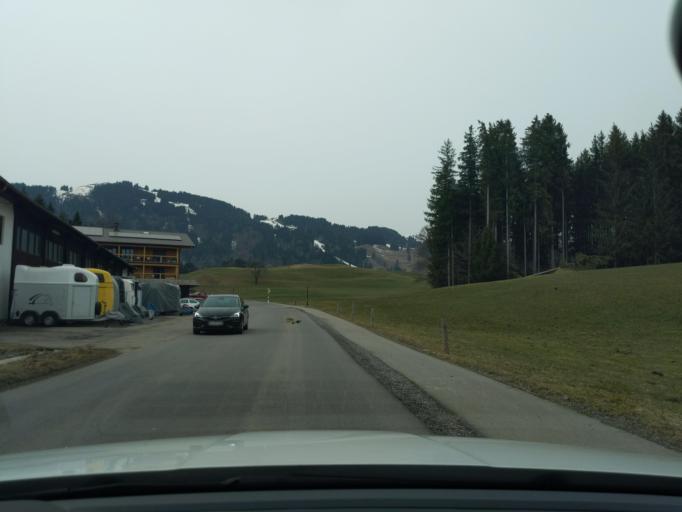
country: DE
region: Bavaria
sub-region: Swabia
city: Ofterschwang
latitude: 47.4886
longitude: 10.2494
